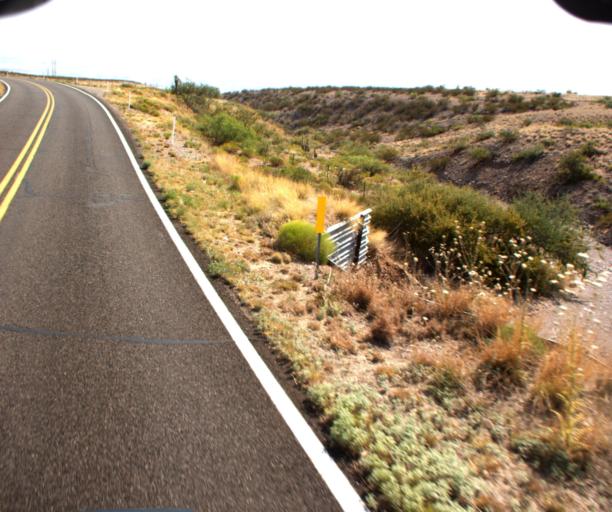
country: US
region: Arizona
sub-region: Greenlee County
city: Clifton
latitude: 32.9867
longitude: -109.1811
